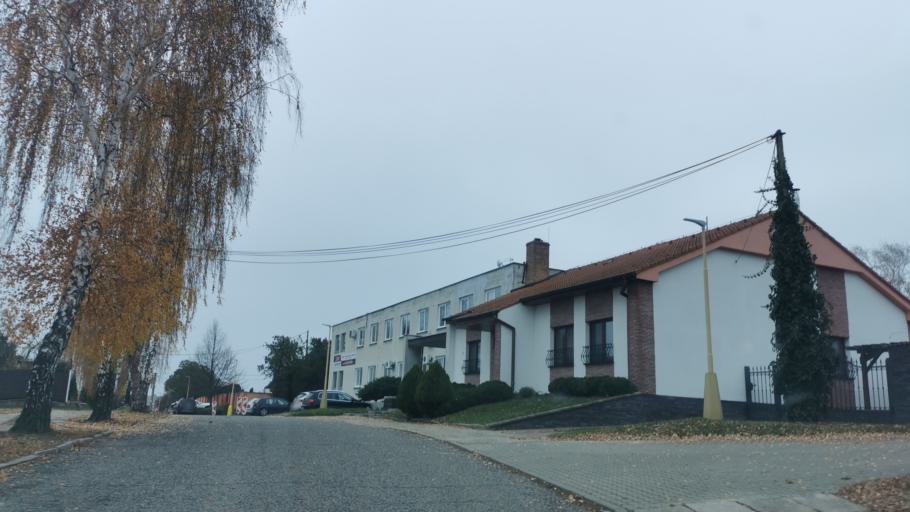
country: SK
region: Trnavsky
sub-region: Okres Skalica
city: Holic
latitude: 48.8148
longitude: 17.1704
